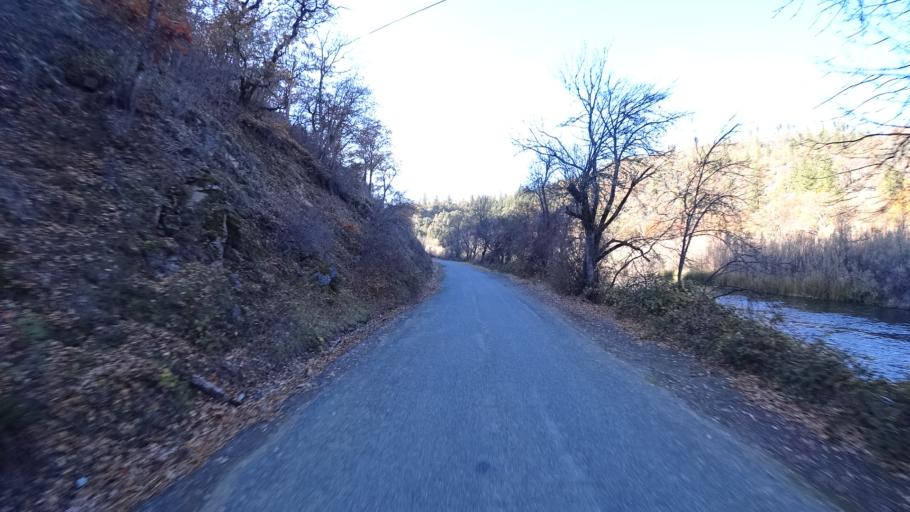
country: US
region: California
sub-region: Siskiyou County
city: Yreka
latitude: 41.8291
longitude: -122.9589
